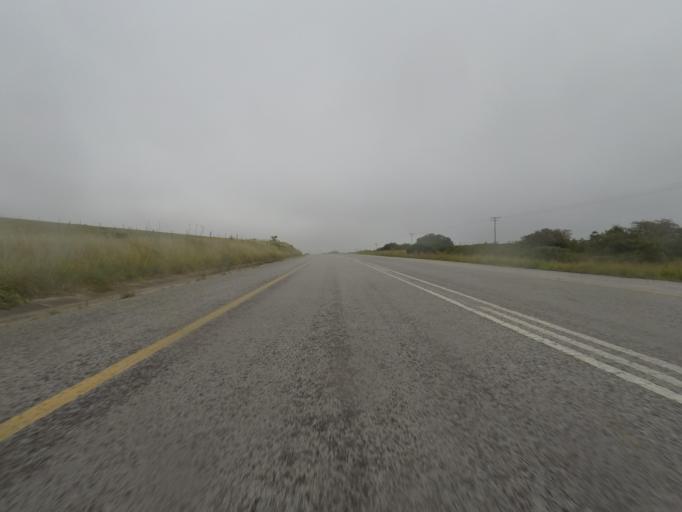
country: ZA
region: Eastern Cape
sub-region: Cacadu District Municipality
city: Grahamstown
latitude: -33.6415
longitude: 26.3311
